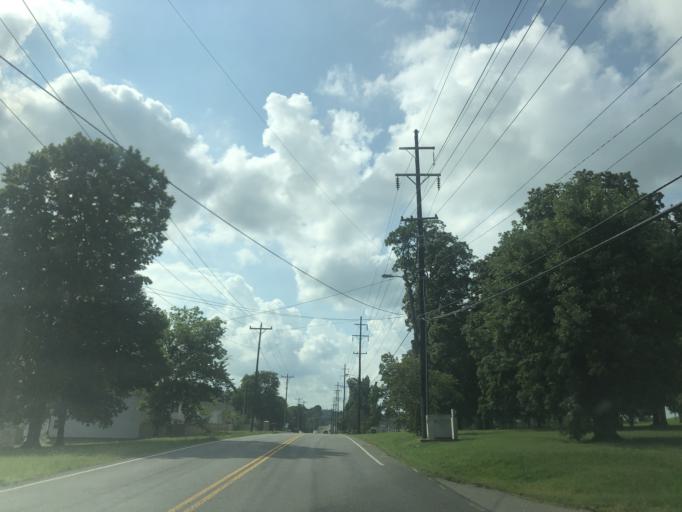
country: US
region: Tennessee
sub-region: Davidson County
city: Lakewood
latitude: 36.1605
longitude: -86.6443
